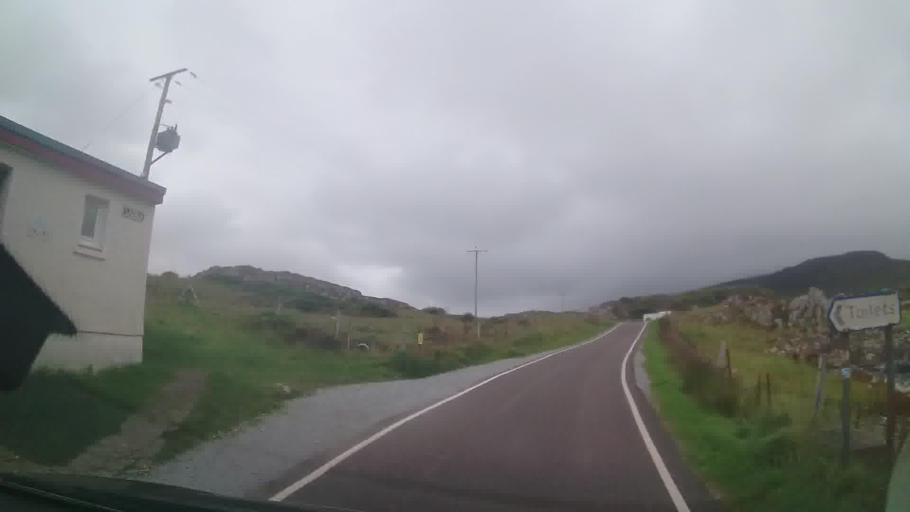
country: GB
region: Scotland
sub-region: Argyll and Bute
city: Isle Of Mull
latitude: 56.6891
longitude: -6.0958
